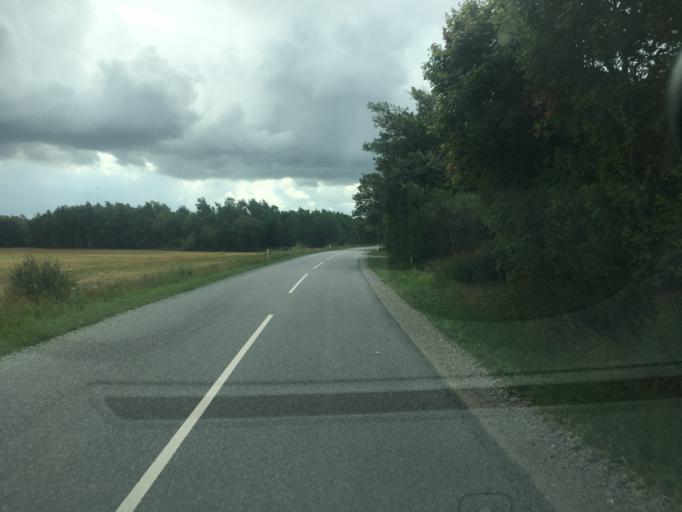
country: DK
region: South Denmark
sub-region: Tonder Kommune
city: Logumkloster
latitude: 55.0300
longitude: 8.9685
